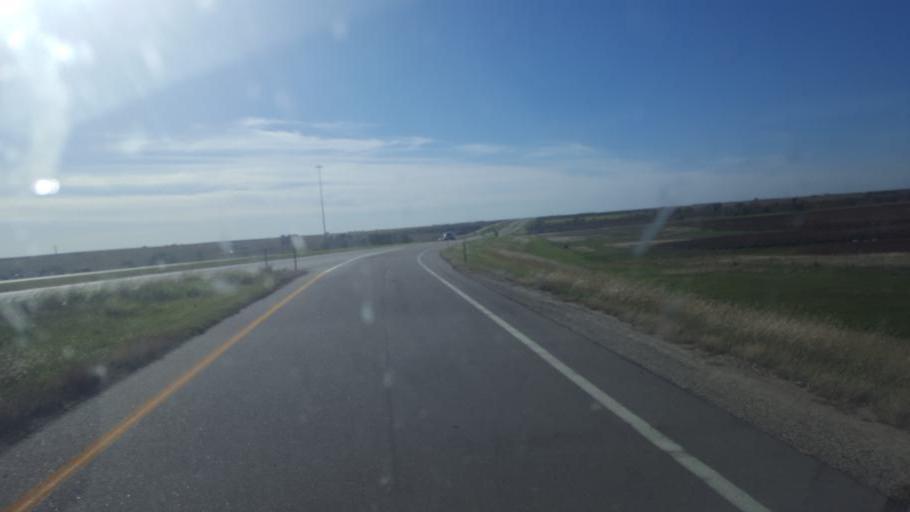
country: US
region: Kansas
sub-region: Russell County
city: Russell
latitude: 38.8576
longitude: -98.7085
